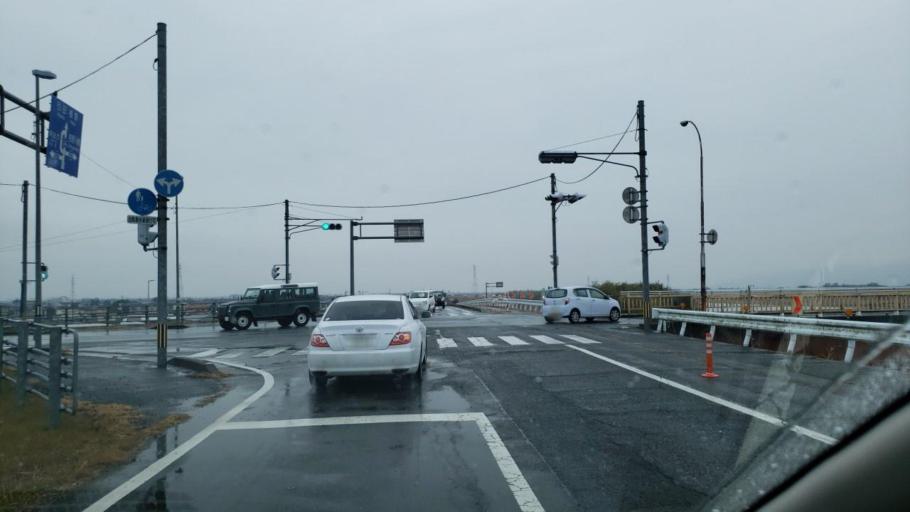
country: JP
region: Tokushima
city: Ishii
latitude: 34.1078
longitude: 134.4367
